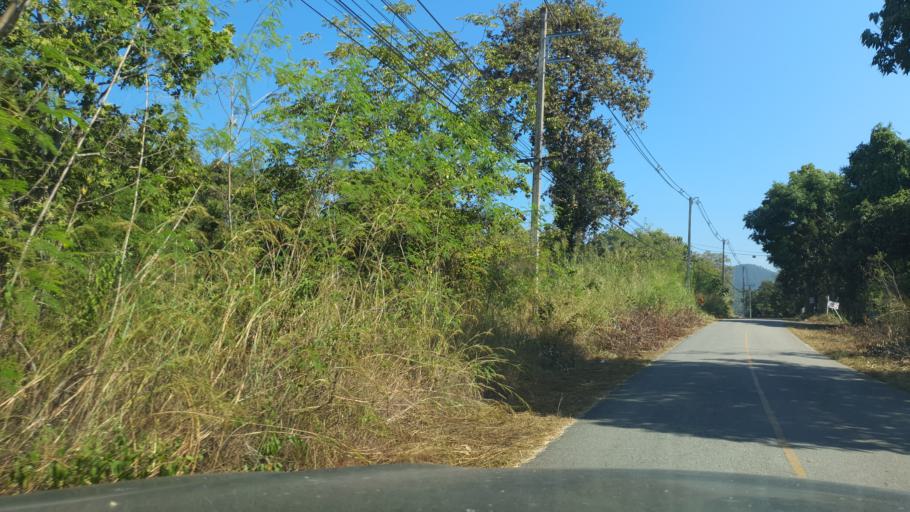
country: TH
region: Chiang Mai
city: San Sai
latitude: 18.8842
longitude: 99.1628
